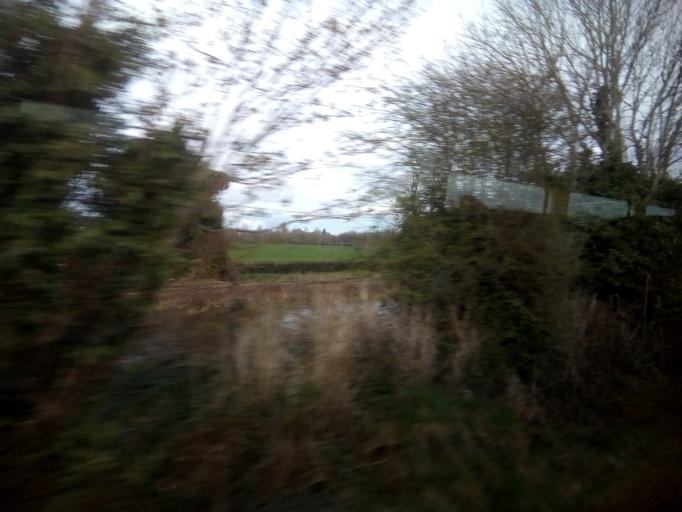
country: IE
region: Leinster
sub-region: Kildare
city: Kilcock
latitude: 53.4210
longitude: -6.7164
